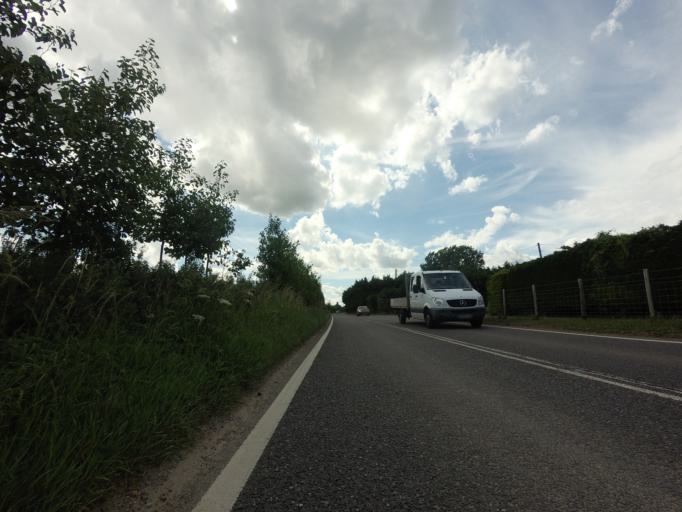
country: GB
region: England
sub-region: Medway
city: Stoke
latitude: 51.4486
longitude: 0.6025
